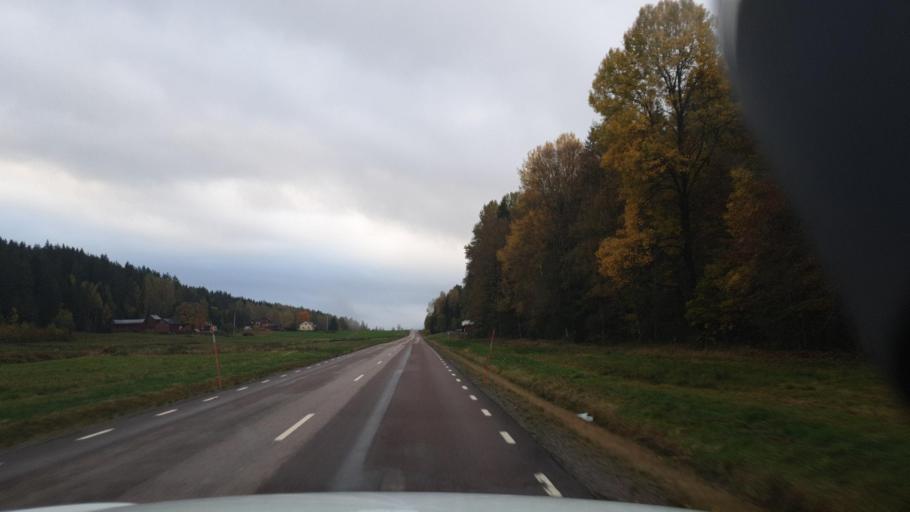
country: SE
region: Vaermland
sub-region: Arvika Kommun
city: Arvika
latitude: 59.7366
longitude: 12.6416
